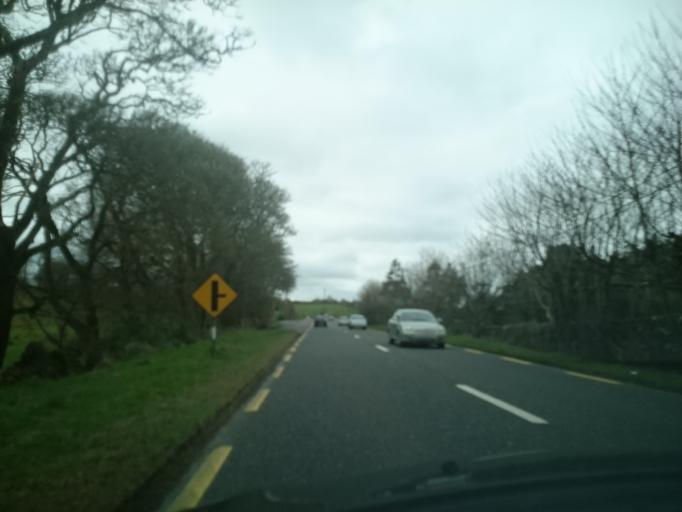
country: IE
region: Connaught
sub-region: Maigh Eo
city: Castlebar
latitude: 53.8184
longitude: -9.3904
